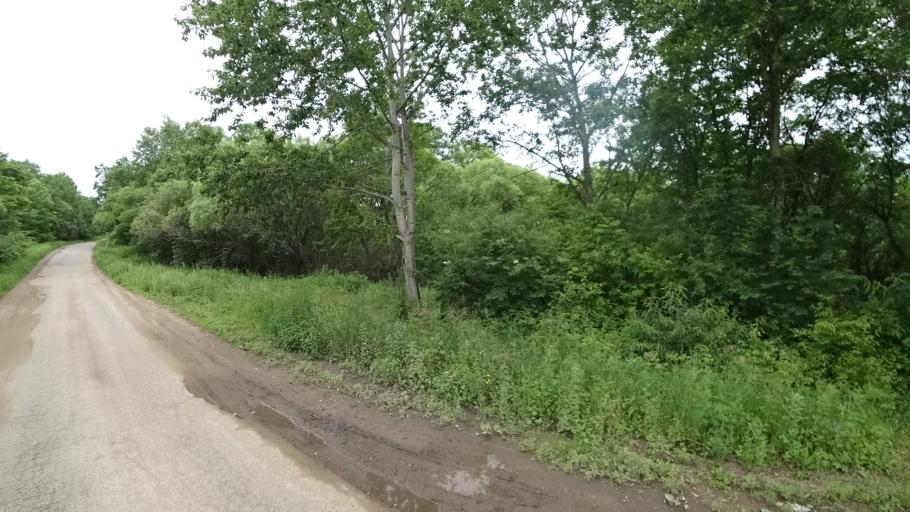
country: RU
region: Primorskiy
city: Novosysoyevka
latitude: 44.2041
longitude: 133.3249
